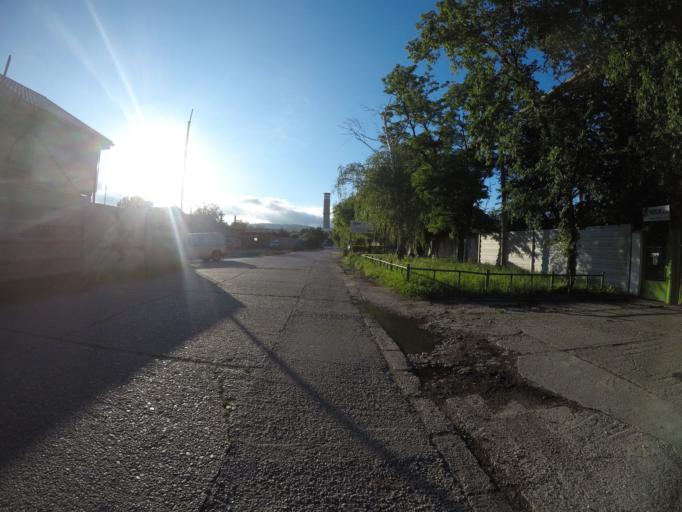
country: SK
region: Bratislavsky
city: Bratislava
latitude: 48.1726
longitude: 17.1531
